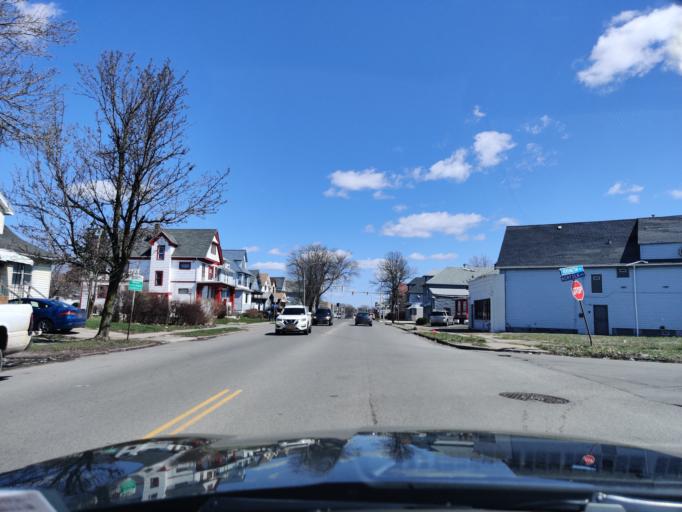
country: US
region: New York
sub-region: Erie County
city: Eggertsville
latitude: 42.9355
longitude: -78.8197
